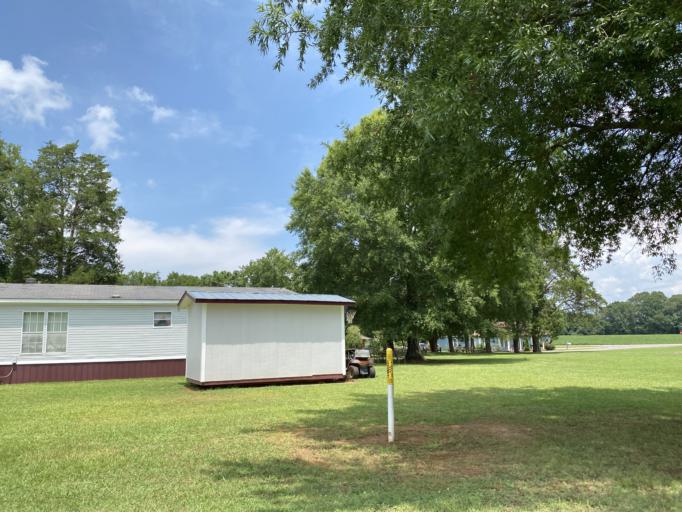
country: US
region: Alabama
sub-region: Lawrence County
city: Town Creek
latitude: 34.6686
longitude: -87.3006
